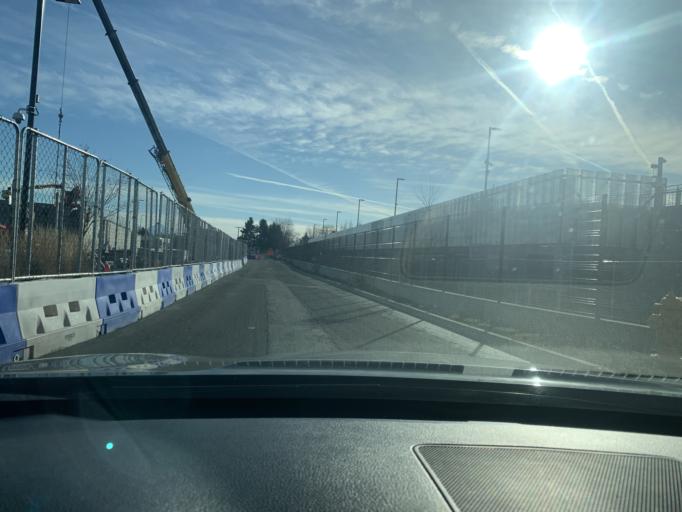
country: US
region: Washington
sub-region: Clark County
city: Walnut Grove
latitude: 45.5865
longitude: -122.5882
